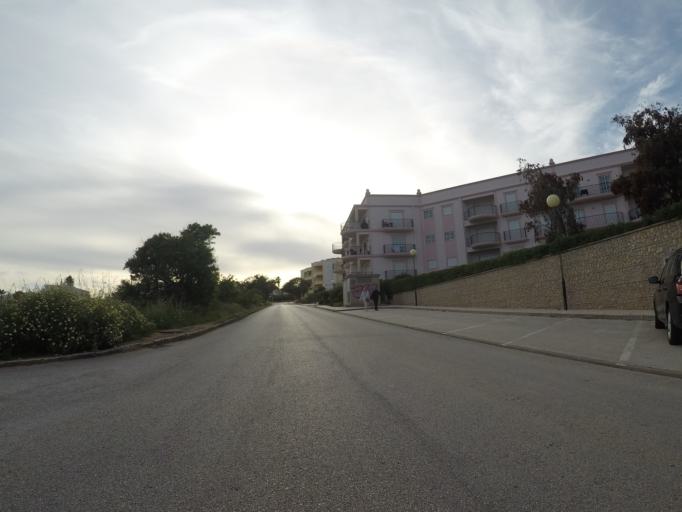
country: PT
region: Faro
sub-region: Lagos
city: Lagos
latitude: 37.0868
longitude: -8.7354
